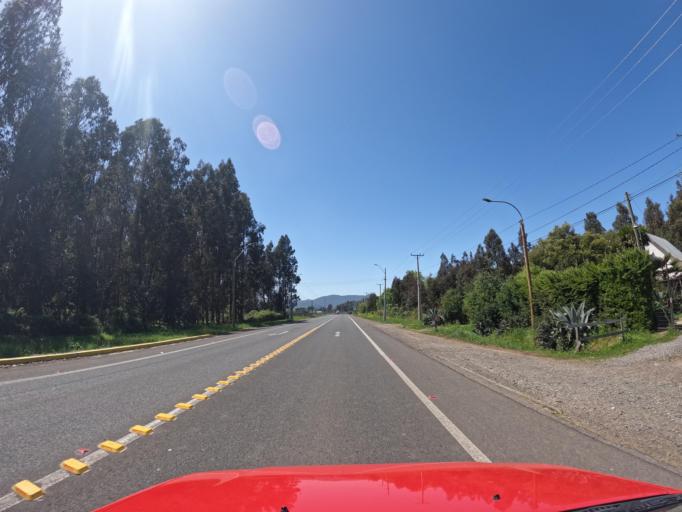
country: CL
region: Maule
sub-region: Provincia de Linares
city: Colbun
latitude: -35.7235
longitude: -71.4167
